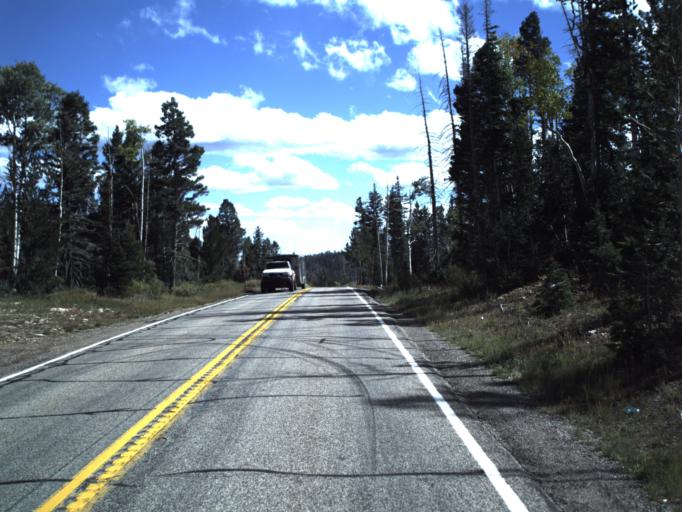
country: US
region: Utah
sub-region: Iron County
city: Parowan
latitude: 37.5302
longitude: -112.7655
